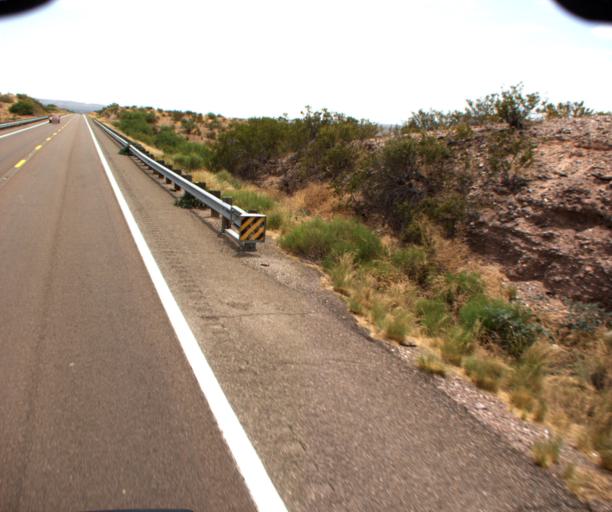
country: US
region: Arizona
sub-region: Graham County
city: Bylas
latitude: 33.2037
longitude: -110.1940
